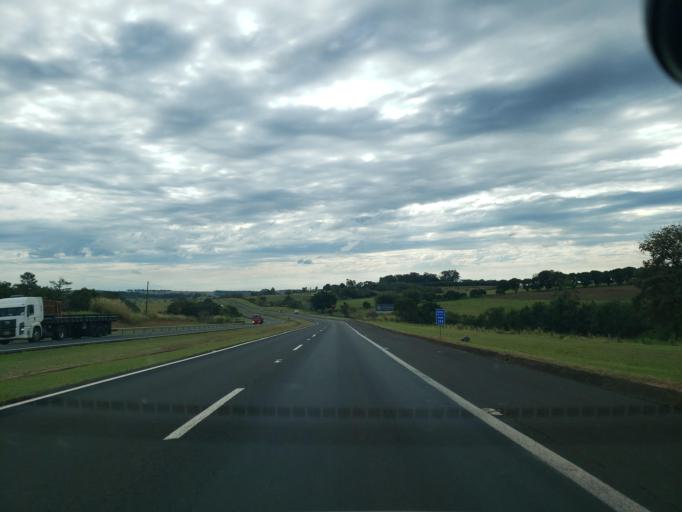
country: BR
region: Sao Paulo
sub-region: Bauru
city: Bauru
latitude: -22.2201
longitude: -49.1664
